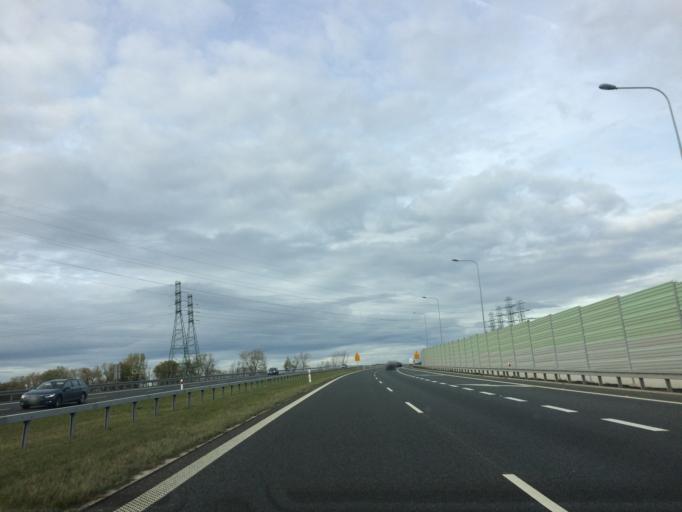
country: PL
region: Lower Silesian Voivodeship
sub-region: Powiat legnicki
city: Milkowice
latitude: 51.1787
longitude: 16.0889
